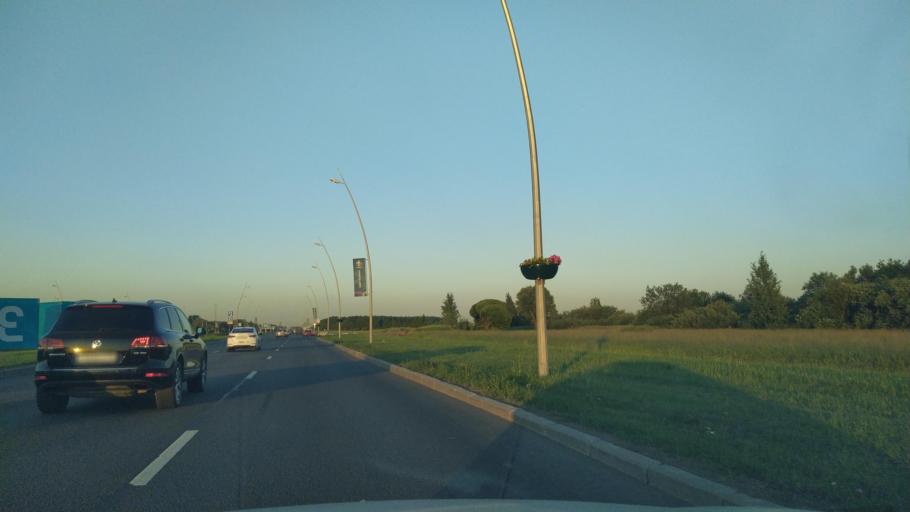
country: RU
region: St.-Petersburg
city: Dachnoye
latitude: 59.7950
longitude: 30.2863
